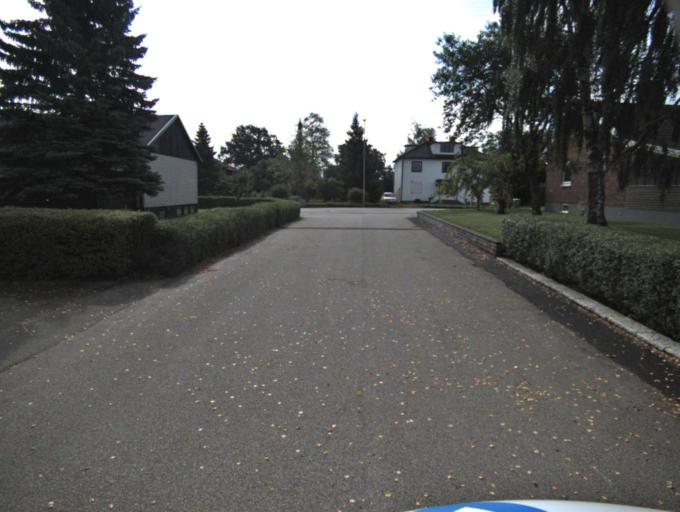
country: SE
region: Vaestra Goetaland
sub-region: Falkopings Kommun
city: Falkoeping
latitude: 57.9845
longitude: 13.5376
